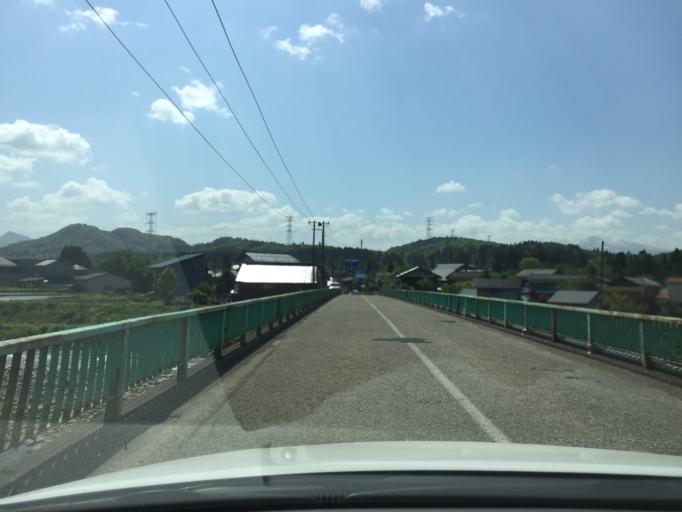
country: JP
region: Niigata
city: Tochio-honcho
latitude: 37.5464
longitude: 139.0906
